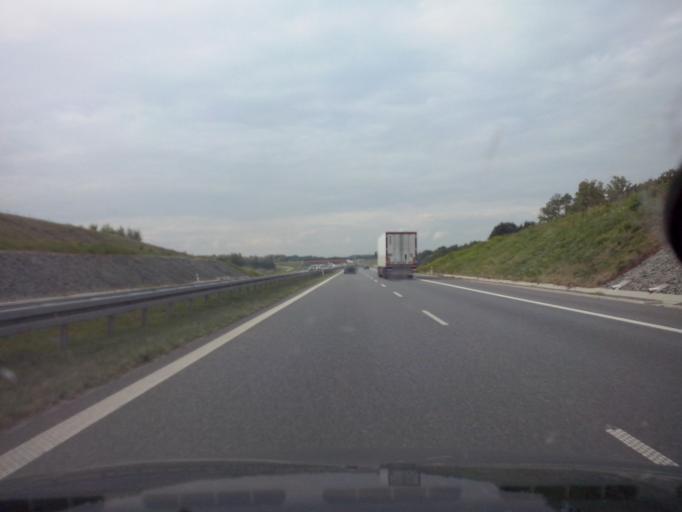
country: PL
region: Lesser Poland Voivodeship
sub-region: Powiat bochenski
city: Jodlowka
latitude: 50.0010
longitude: 20.5510
